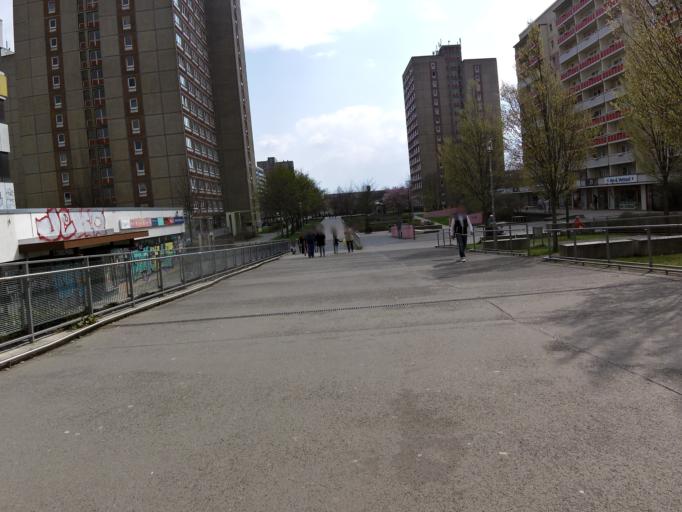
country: DE
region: Saxony
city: Markranstadt
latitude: 51.3183
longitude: 12.2905
